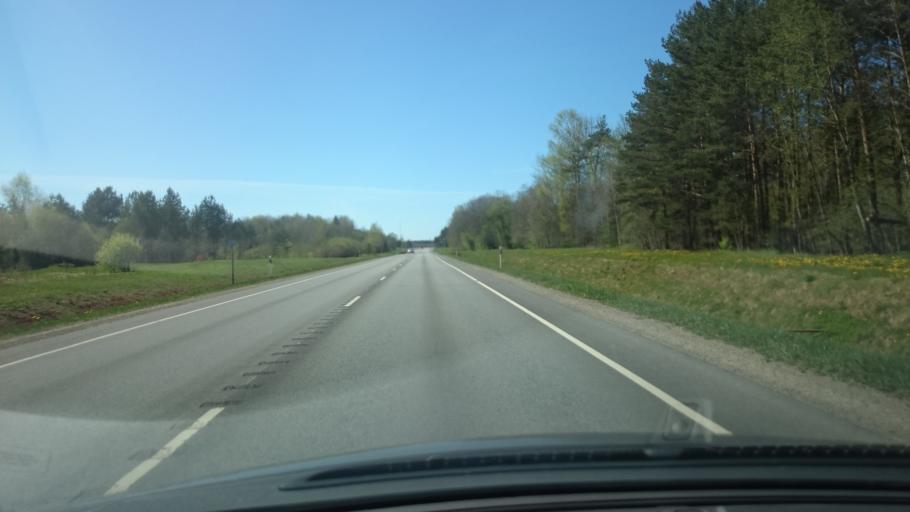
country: EE
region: Ida-Virumaa
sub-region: Johvi vald
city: Johvi
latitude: 59.3649
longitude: 27.4450
